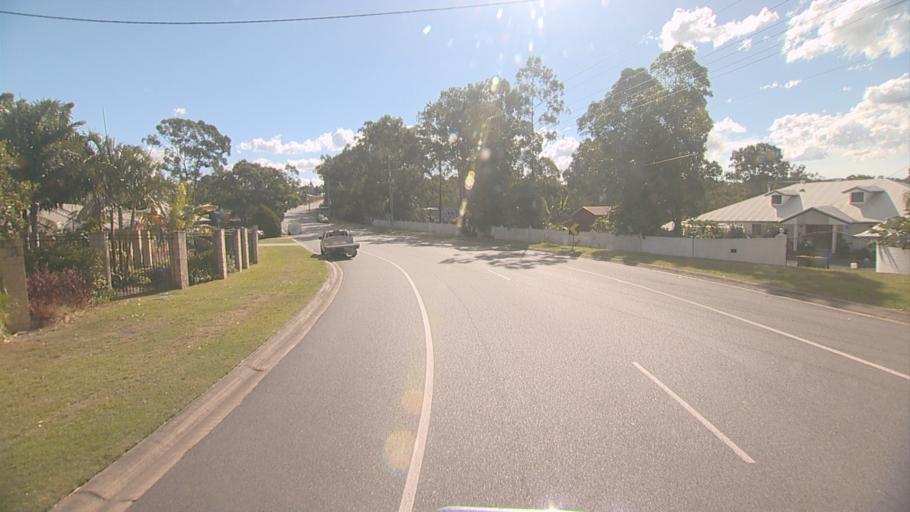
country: AU
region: Queensland
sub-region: Gold Coast
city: Yatala
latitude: -27.6742
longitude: 153.2267
